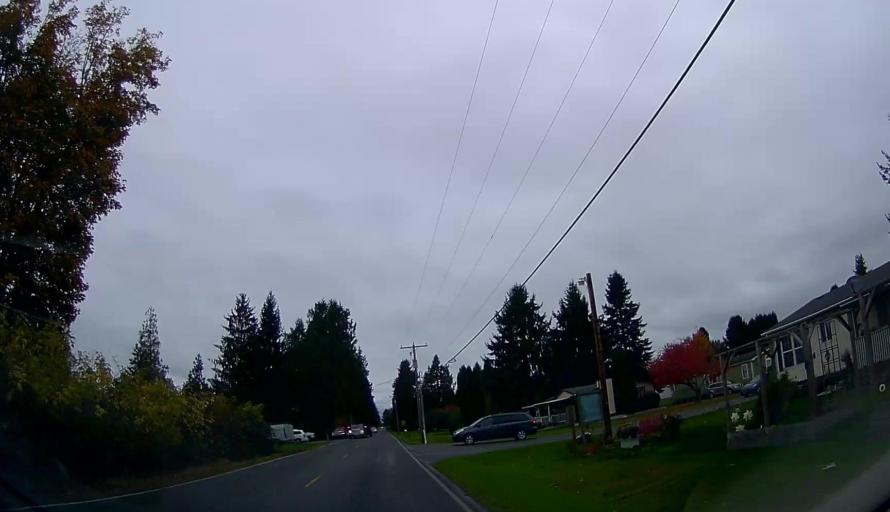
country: US
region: Washington
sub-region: Skagit County
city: Sedro-Woolley
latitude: 48.5032
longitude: -122.2058
